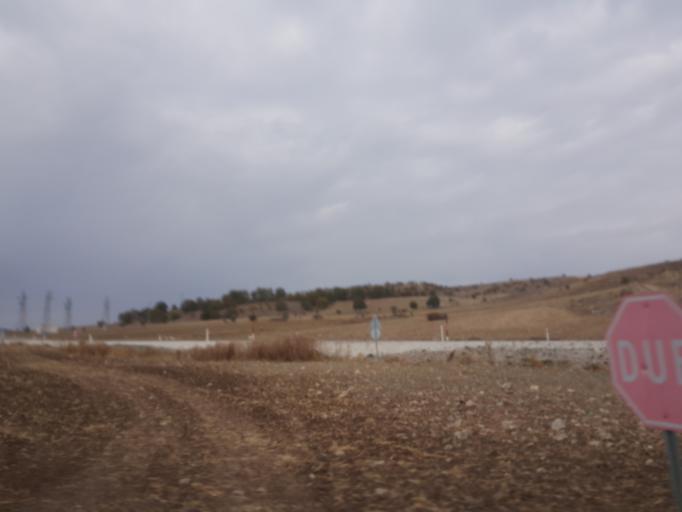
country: TR
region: Corum
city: Cemilbey
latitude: 40.2691
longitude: 35.0743
